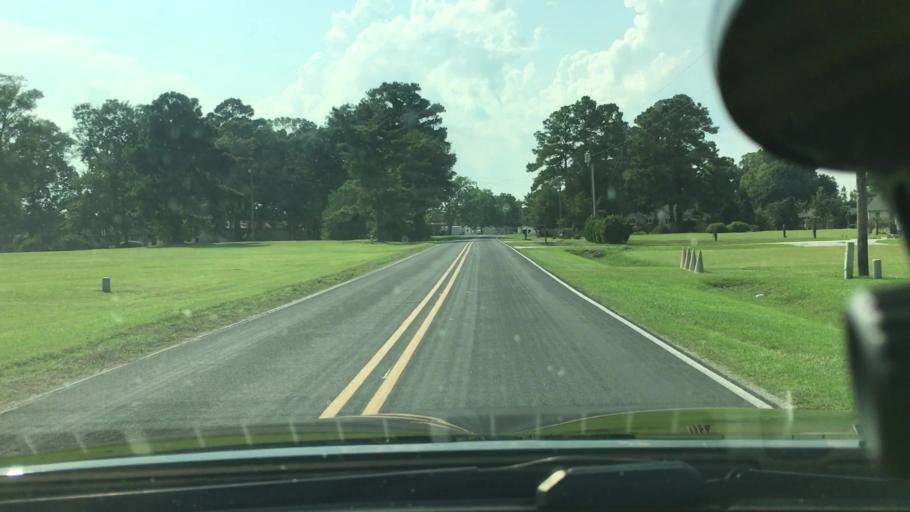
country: US
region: North Carolina
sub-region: Craven County
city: New Bern
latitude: 35.1581
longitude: -77.0427
